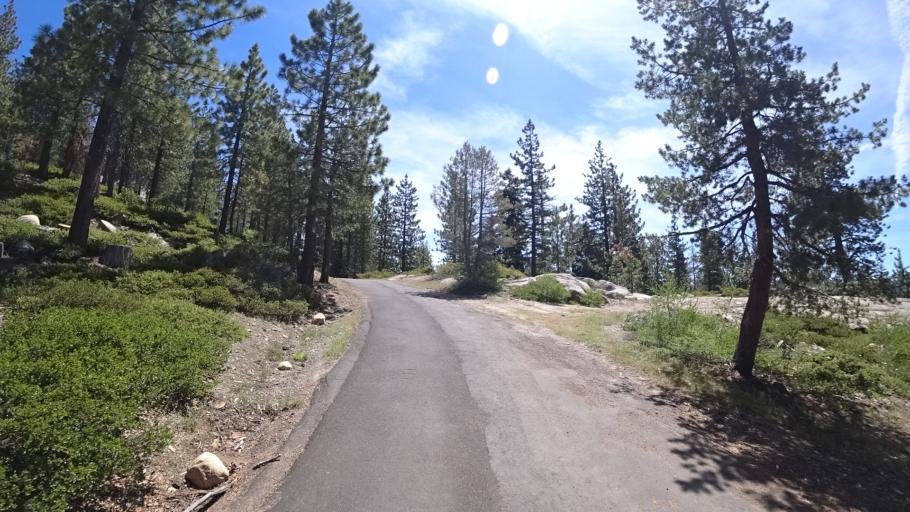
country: US
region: California
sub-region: Calaveras County
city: Arnold
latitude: 38.4232
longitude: -120.0965
